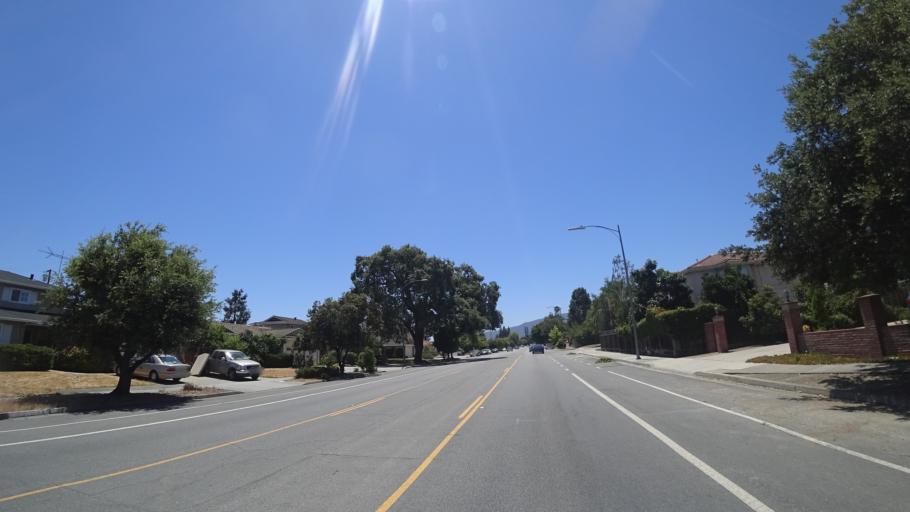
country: US
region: California
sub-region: Santa Clara County
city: Cupertino
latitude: 37.2974
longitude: -122.0151
